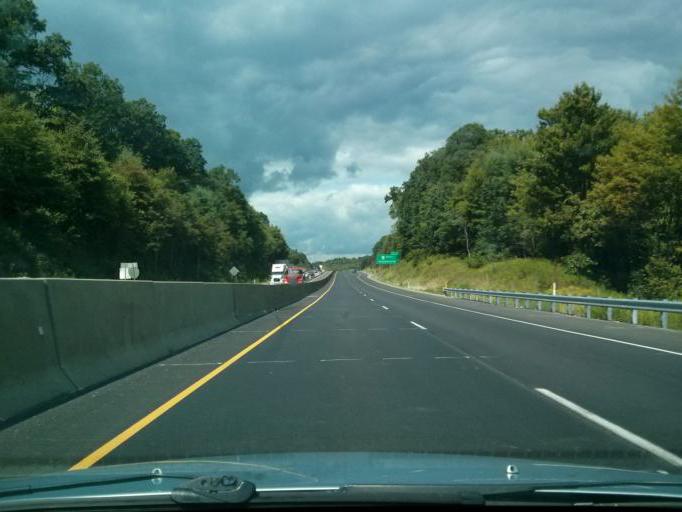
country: US
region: Pennsylvania
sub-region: Clarion County
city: Clarion
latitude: 41.1895
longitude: -79.4175
